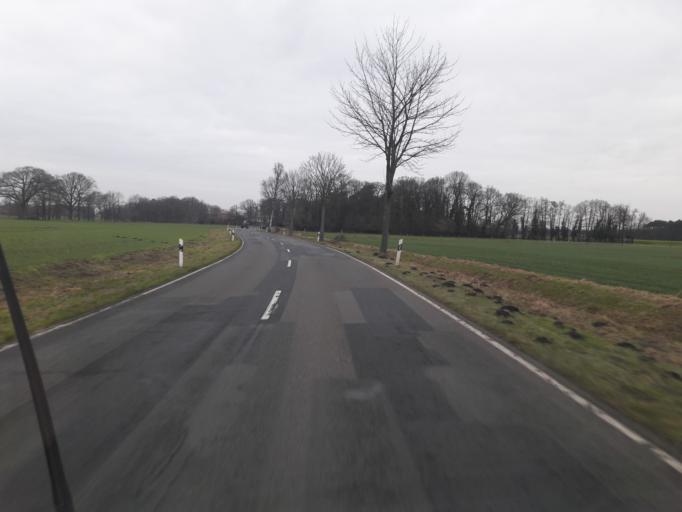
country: DE
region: Lower Saxony
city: Warmsen
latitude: 52.4057
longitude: 8.8602
